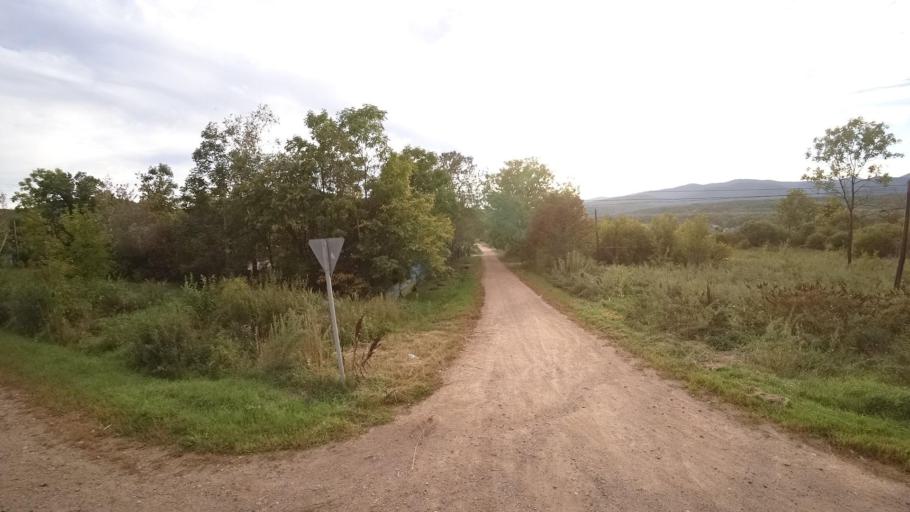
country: RU
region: Primorskiy
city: Yakovlevka
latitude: 44.4135
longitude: 133.4536
